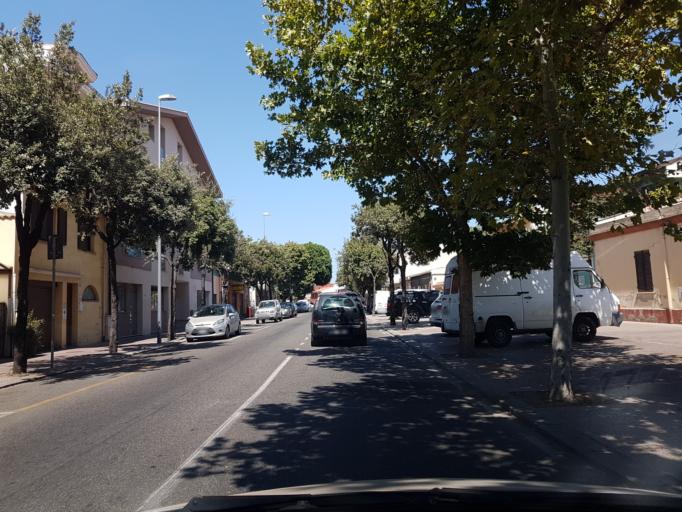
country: IT
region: Sardinia
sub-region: Provincia di Oristano
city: Oristano
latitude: 39.8976
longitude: 8.5948
